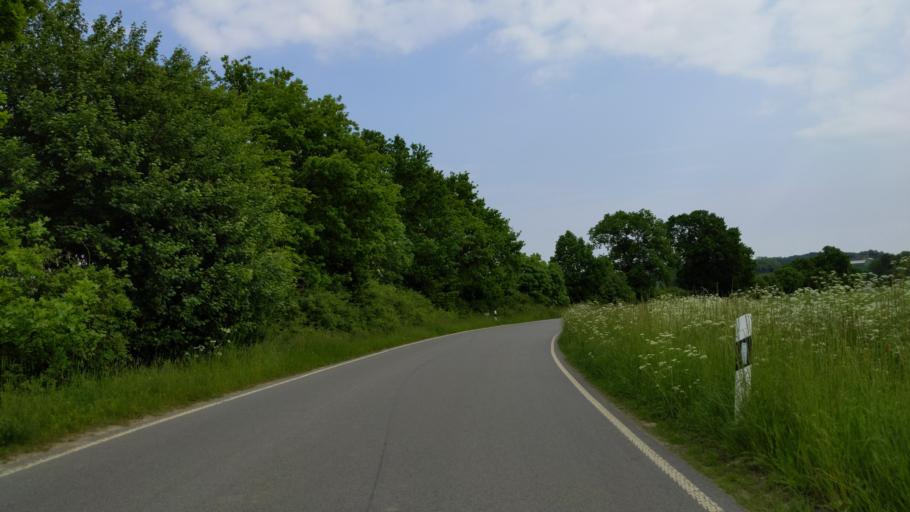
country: DE
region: Schleswig-Holstein
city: Bad Schwartau
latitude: 53.9679
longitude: 10.6647
